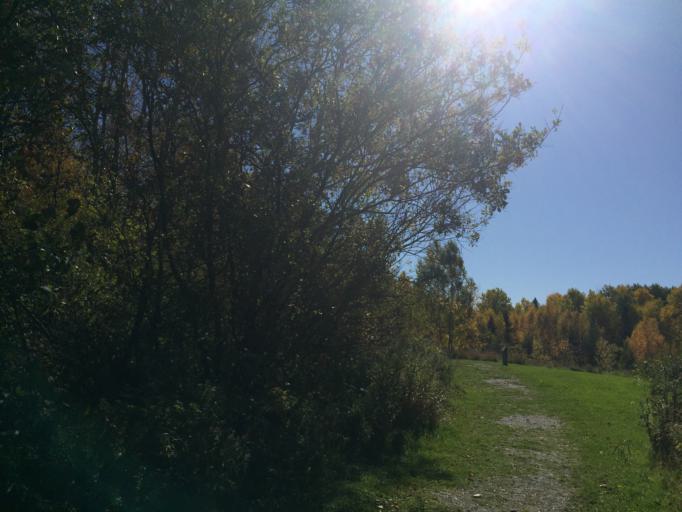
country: US
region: Minnesota
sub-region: Lake of the Woods County
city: Baudette
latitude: 48.2870
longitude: -94.5661
